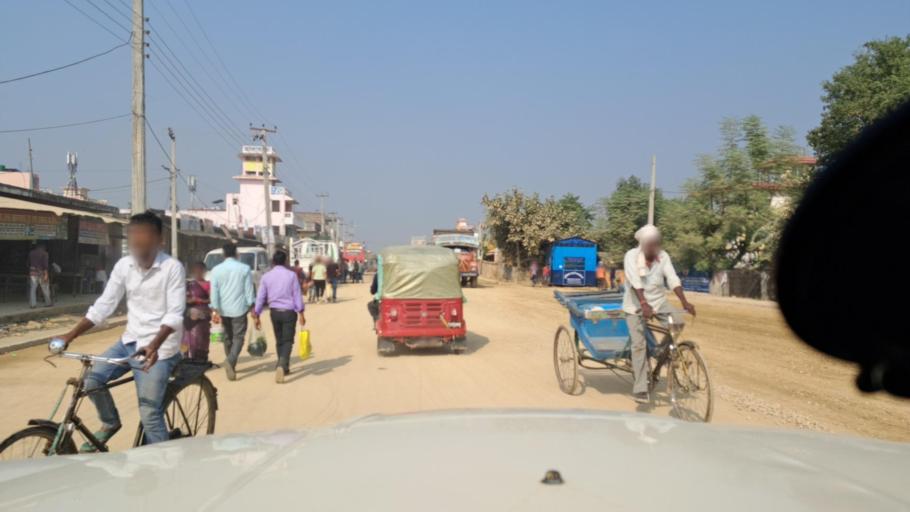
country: IN
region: Uttar Pradesh
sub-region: Balrampur
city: Pachperwa
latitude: 27.5000
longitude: 82.7936
